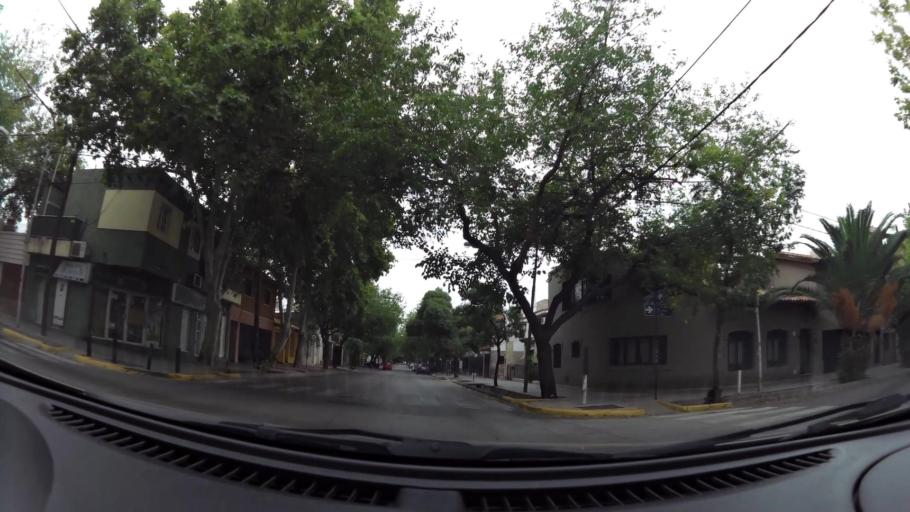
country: AR
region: Mendoza
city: Mendoza
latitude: -32.8916
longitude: -68.8594
